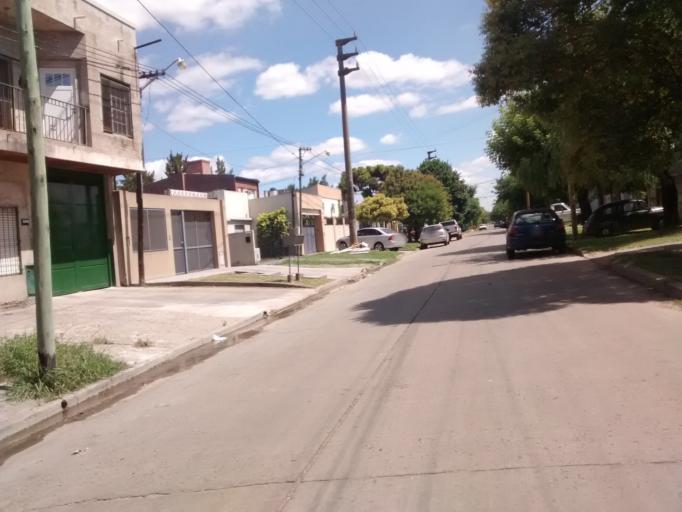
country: AR
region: Buenos Aires
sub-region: Partido de La Plata
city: La Plata
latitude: -34.9231
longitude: -58.0019
